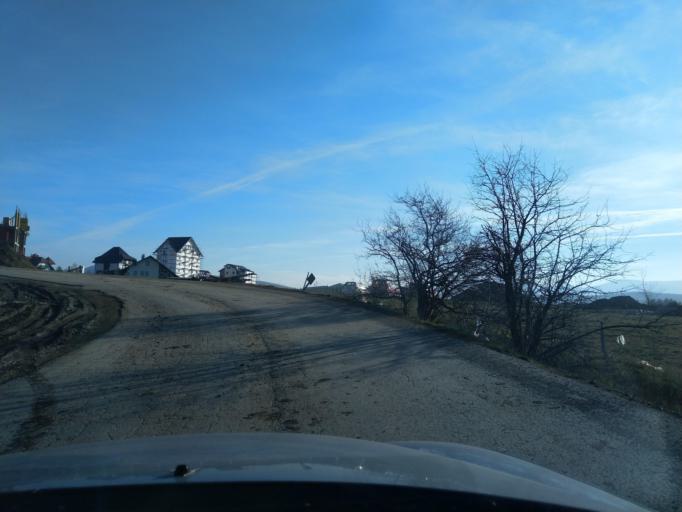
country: RS
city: Zlatibor
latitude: 43.7275
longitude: 19.6819
